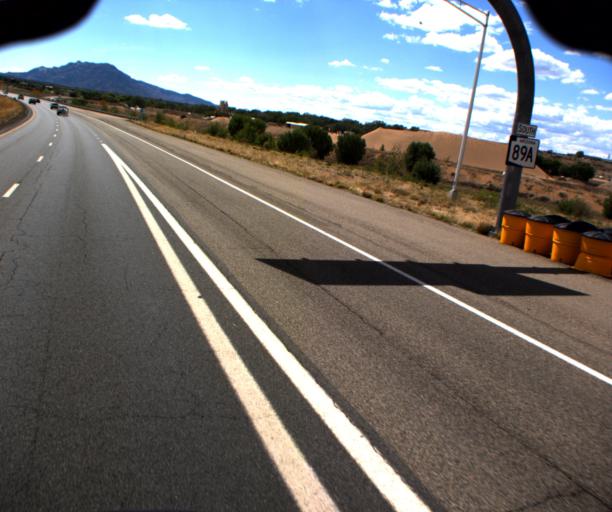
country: US
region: Arizona
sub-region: Yavapai County
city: Prescott Valley
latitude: 34.6374
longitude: -112.4068
